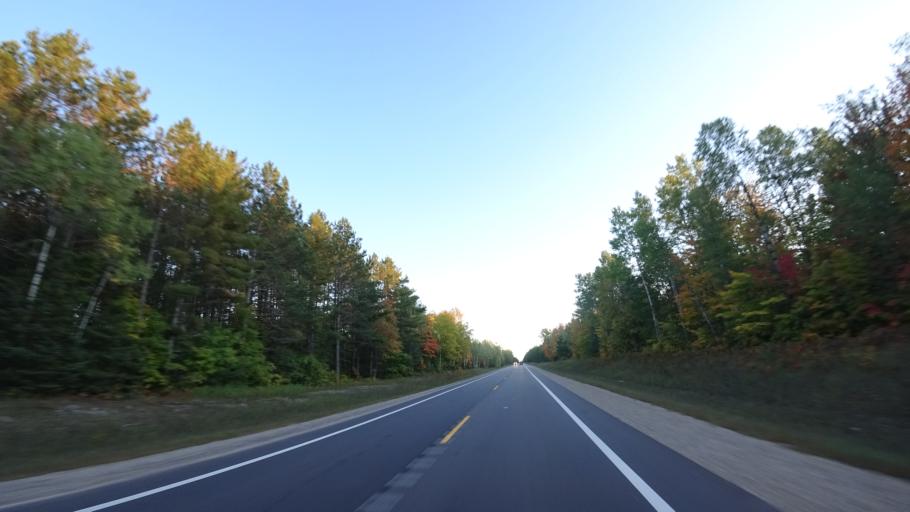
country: US
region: Michigan
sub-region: Luce County
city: Newberry
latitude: 46.3110
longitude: -85.0094
